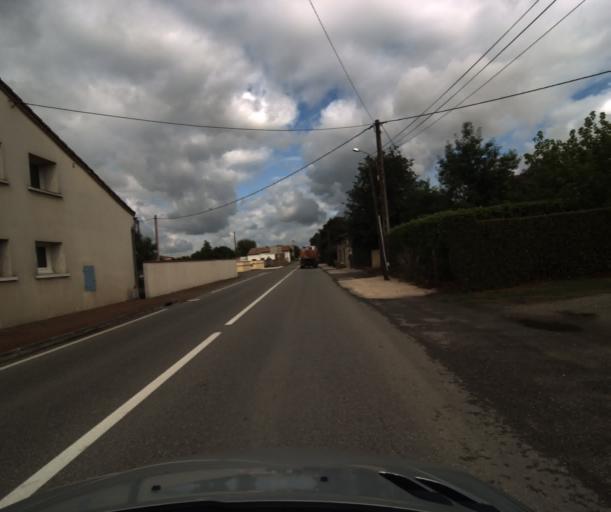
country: FR
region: Midi-Pyrenees
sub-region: Departement du Tarn-et-Garonne
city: Castelsarrasin
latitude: 44.0200
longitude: 1.0701
